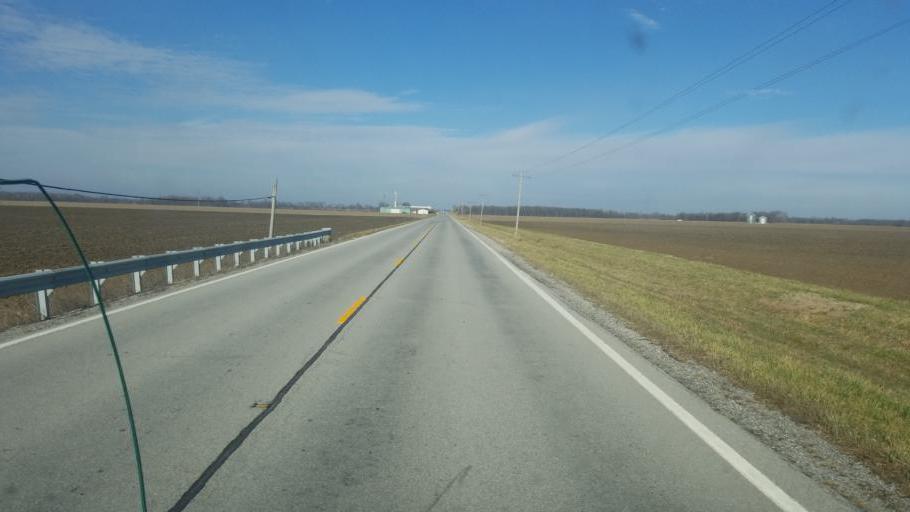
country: US
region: Illinois
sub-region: Saline County
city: Eldorado
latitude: 37.8638
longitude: -88.4529
